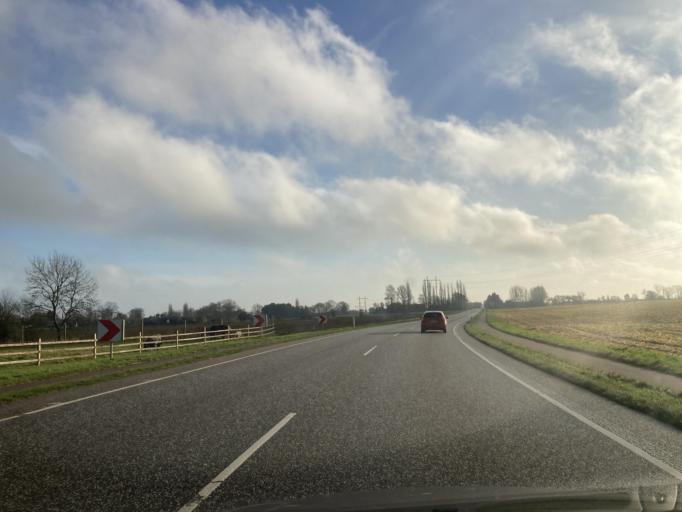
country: DK
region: Zealand
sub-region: Guldborgsund Kommune
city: Sundby
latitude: 54.7696
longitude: 11.7552
